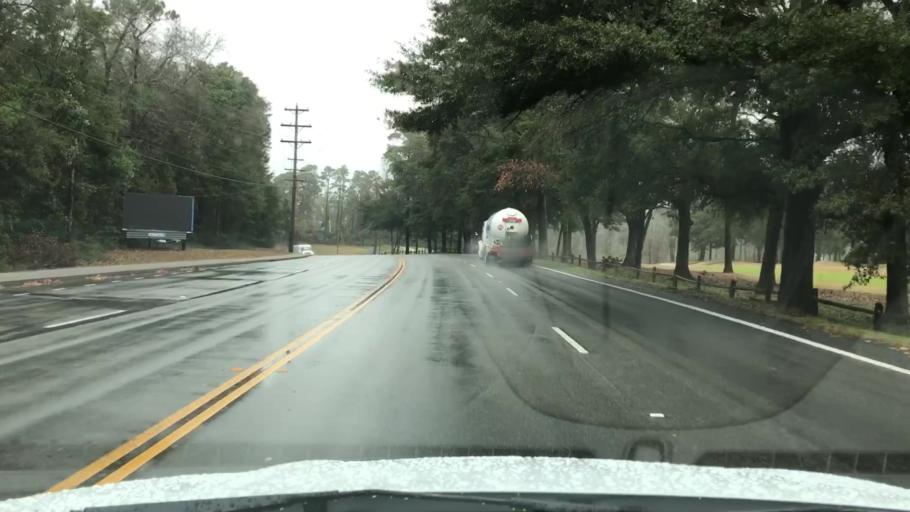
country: US
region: South Carolina
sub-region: Horry County
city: North Myrtle Beach
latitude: 33.7713
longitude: -78.7893
